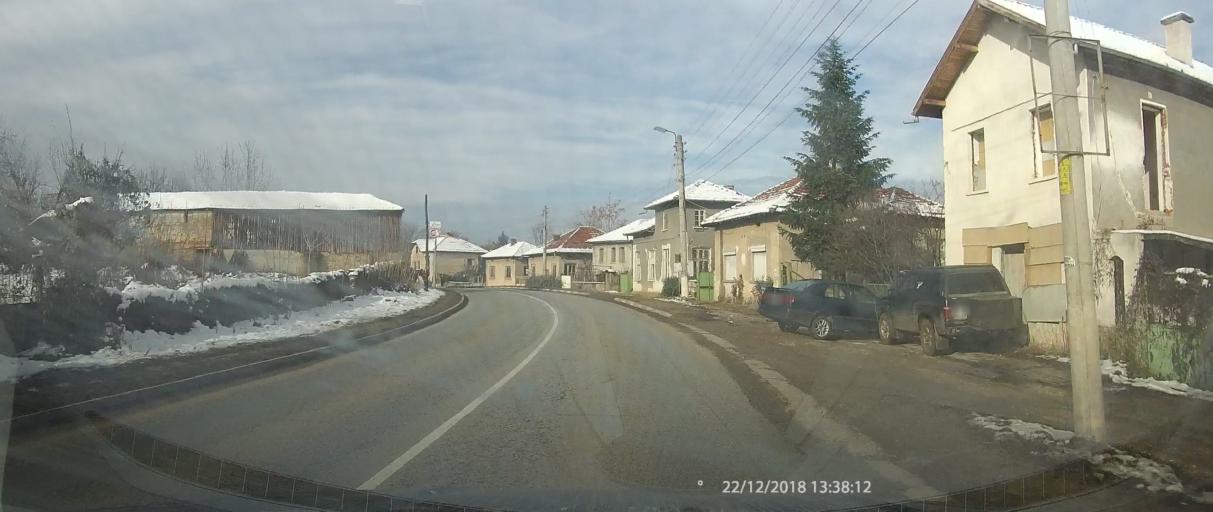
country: BG
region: Lovech
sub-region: Obshtina Lukovit
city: Lukovit
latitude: 43.1530
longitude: 24.1530
